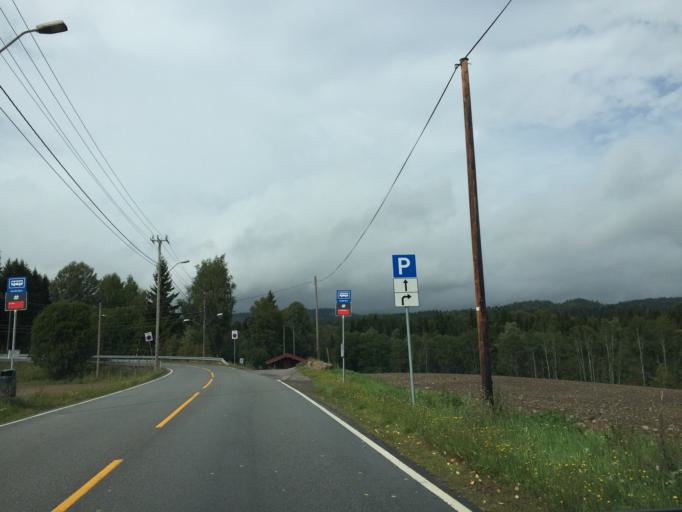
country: NO
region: Akershus
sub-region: Baerum
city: Lysaker
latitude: 60.0186
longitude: 10.5864
